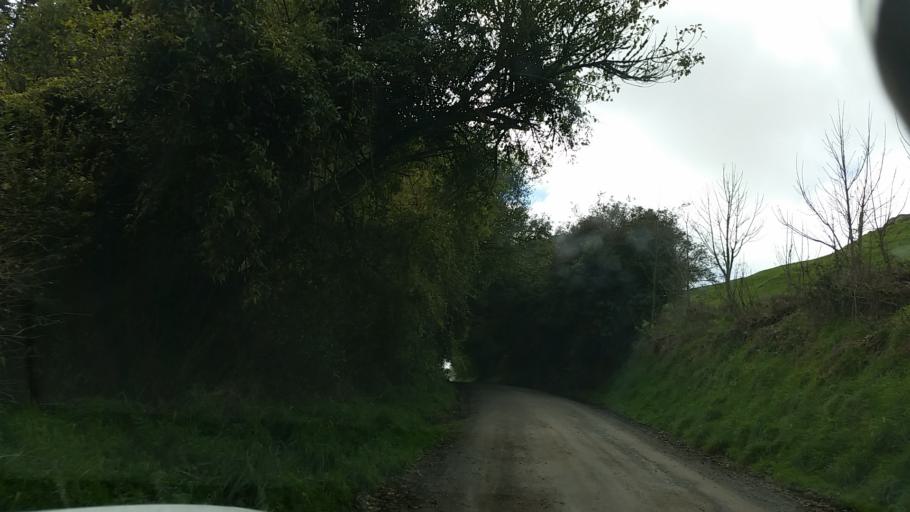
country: NZ
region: Bay of Plenty
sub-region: Rotorua District
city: Rotorua
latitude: -38.2464
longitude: 176.3389
